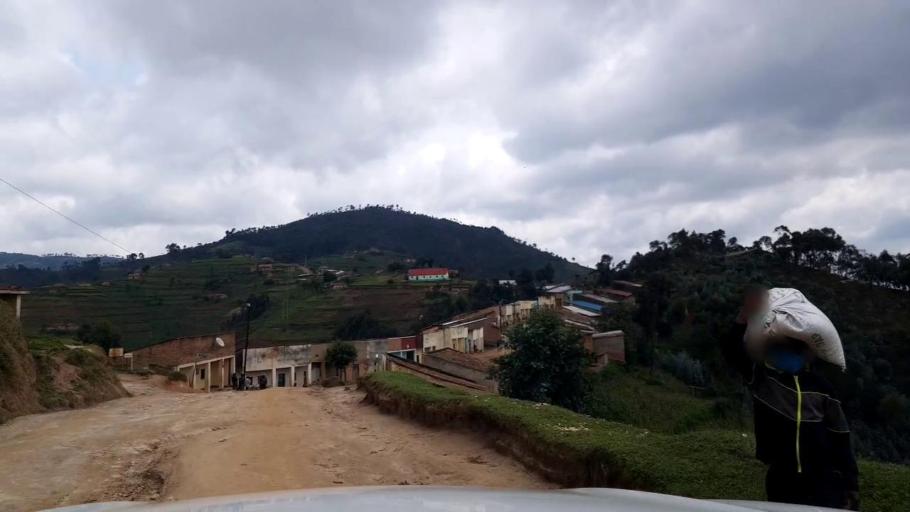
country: RW
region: Western Province
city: Kibuye
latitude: -1.9474
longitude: 29.4724
